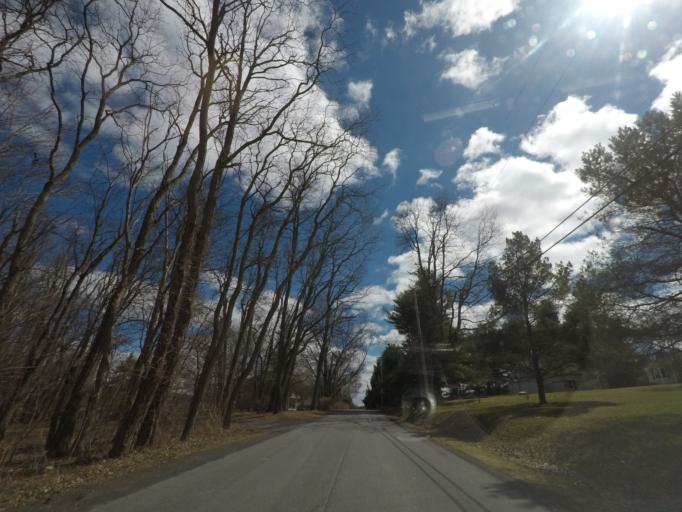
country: US
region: New York
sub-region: Albany County
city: Voorheesville
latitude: 42.6158
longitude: -73.9603
